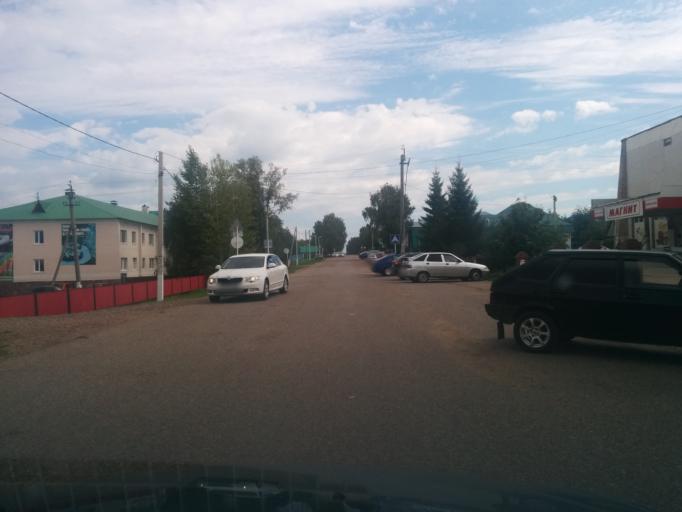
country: RU
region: Bashkortostan
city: Ulukulevo
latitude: 54.4094
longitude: 56.7829
